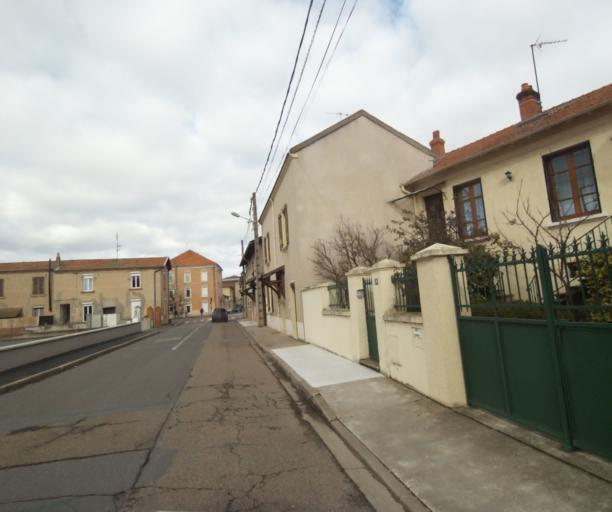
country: FR
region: Rhone-Alpes
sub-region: Departement de la Loire
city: Riorges
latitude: 46.0422
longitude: 4.0529
